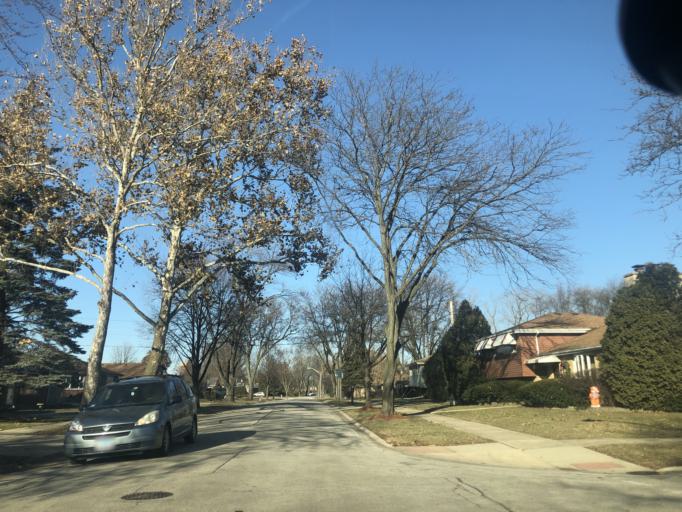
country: US
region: Illinois
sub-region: DuPage County
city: Addison
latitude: 41.9382
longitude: -87.9929
